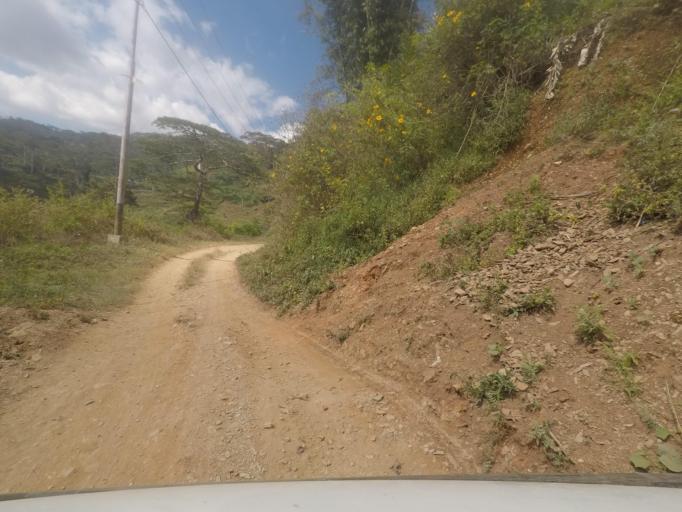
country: TL
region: Ermera
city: Gleno
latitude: -8.7520
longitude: 125.3234
